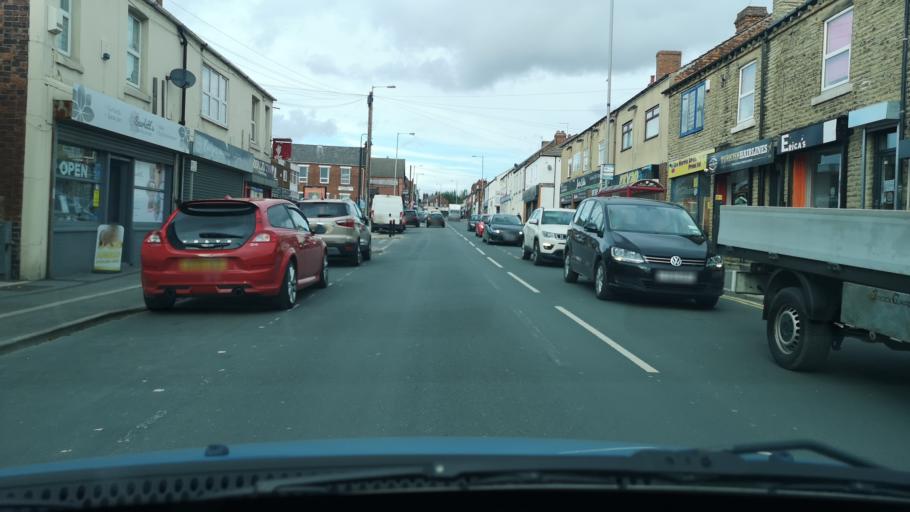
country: GB
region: England
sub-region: City and Borough of Wakefield
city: Featherstone
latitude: 53.6766
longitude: -1.3588
